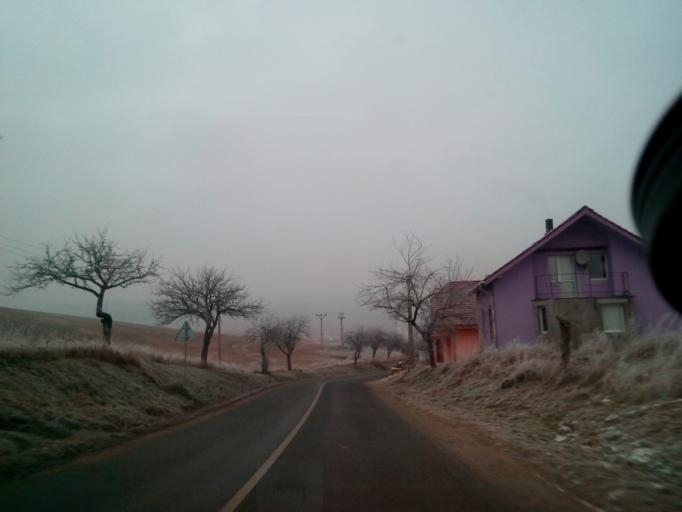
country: SK
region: Presovsky
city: Lubica
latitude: 48.9983
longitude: 20.4555
